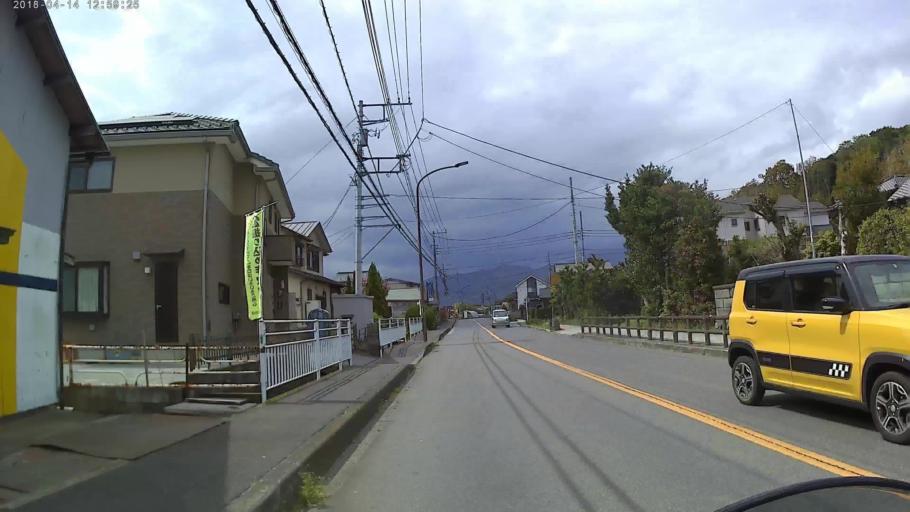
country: JP
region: Kanagawa
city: Isehara
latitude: 35.3698
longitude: 139.3102
